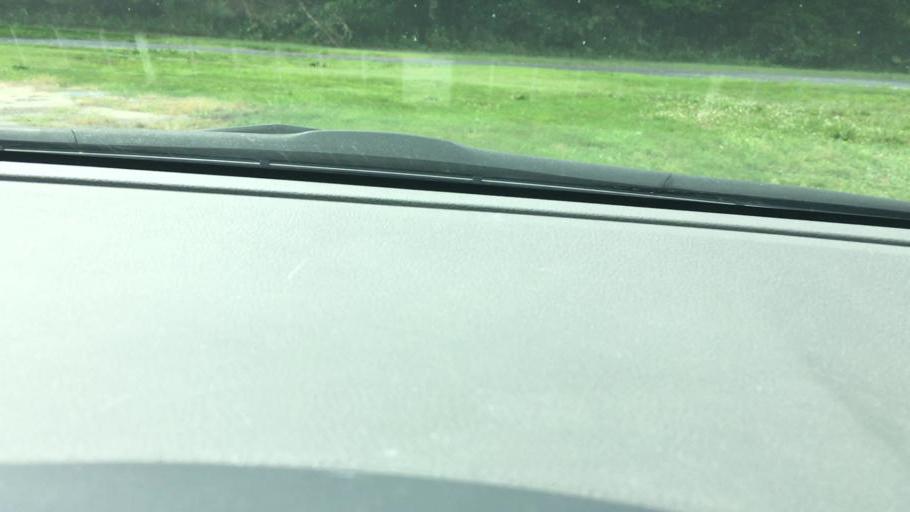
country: US
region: Maryland
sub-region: Worcester County
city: Pocomoke City
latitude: 38.0612
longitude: -75.5027
